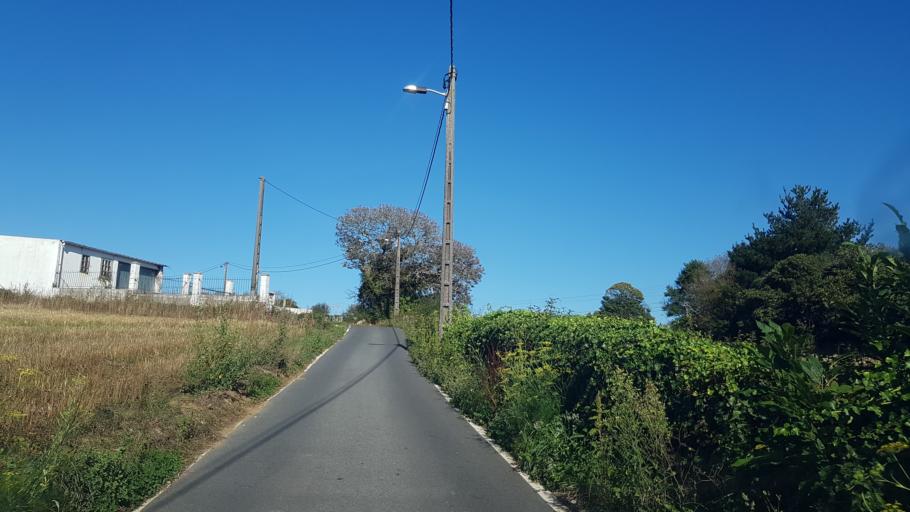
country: ES
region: Galicia
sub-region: Provincia de Lugo
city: Lugo
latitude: 43.0131
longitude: -7.5784
